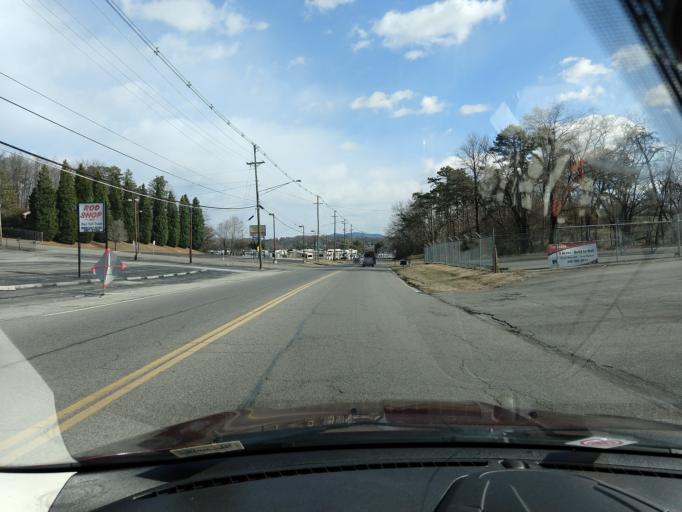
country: US
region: Virginia
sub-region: City of Salem
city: Salem
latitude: 37.2965
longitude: -80.0389
